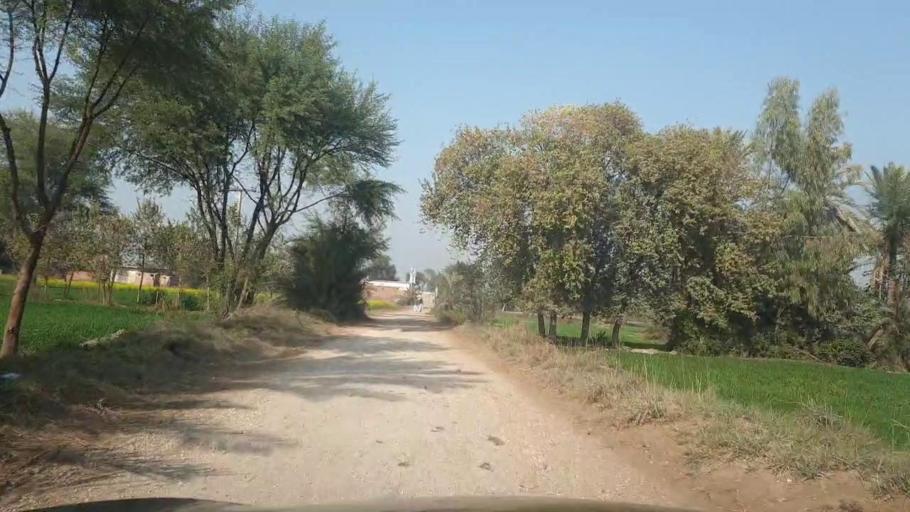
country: PK
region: Sindh
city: Ubauro
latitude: 28.0945
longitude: 69.8412
